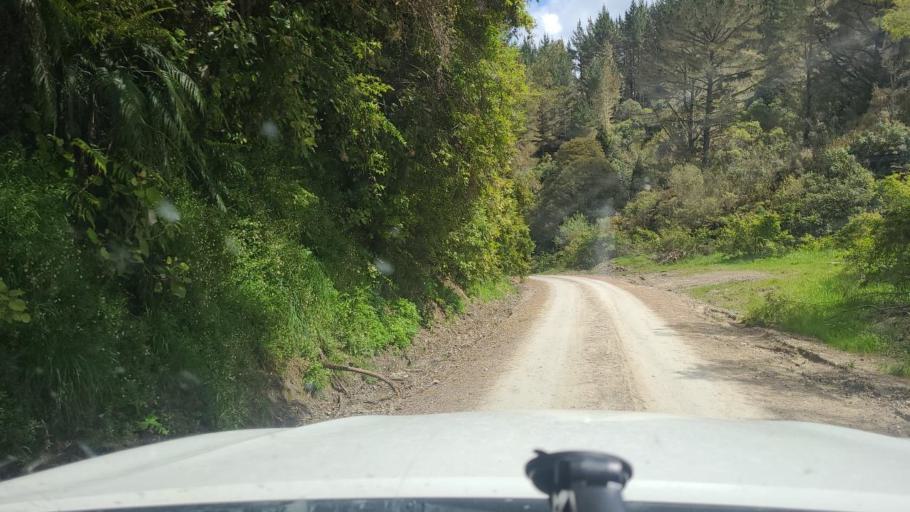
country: NZ
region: Gisborne
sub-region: Gisborne District
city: Gisborne
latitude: -38.8295
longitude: 177.7487
